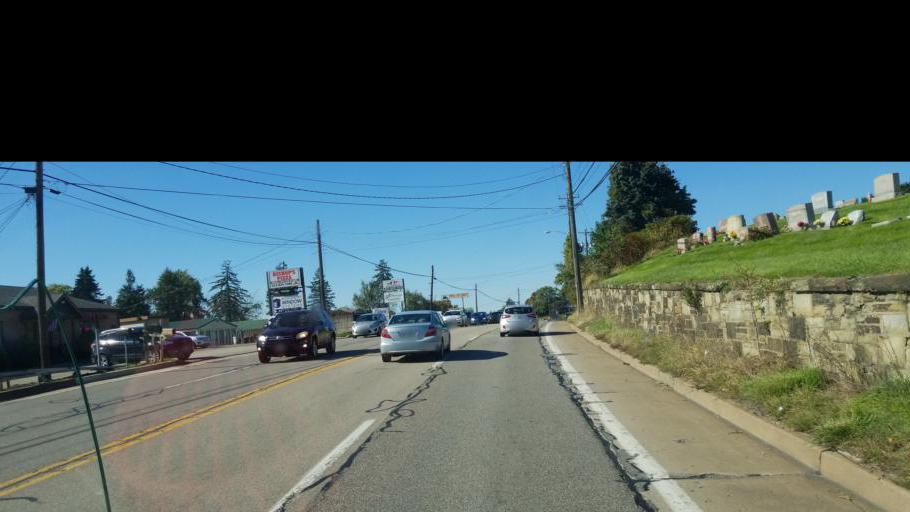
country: US
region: Pennsylvania
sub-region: Allegheny County
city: East McKeesport
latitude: 40.3739
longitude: -79.7947
